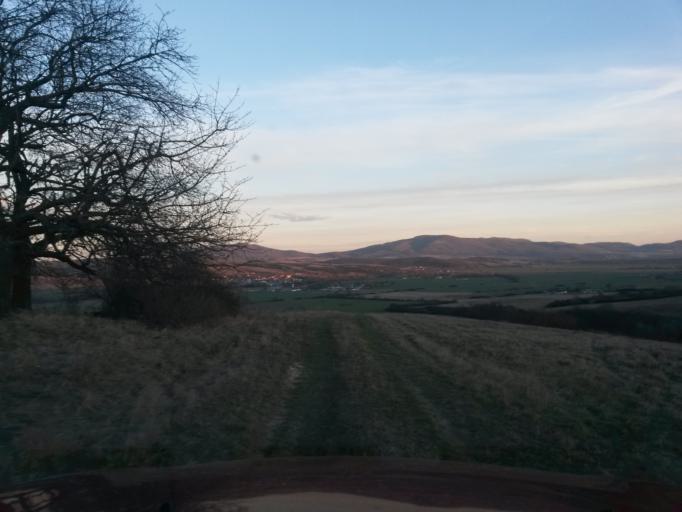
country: SK
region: Kosicky
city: Kosice
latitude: 48.7059
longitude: 21.3132
